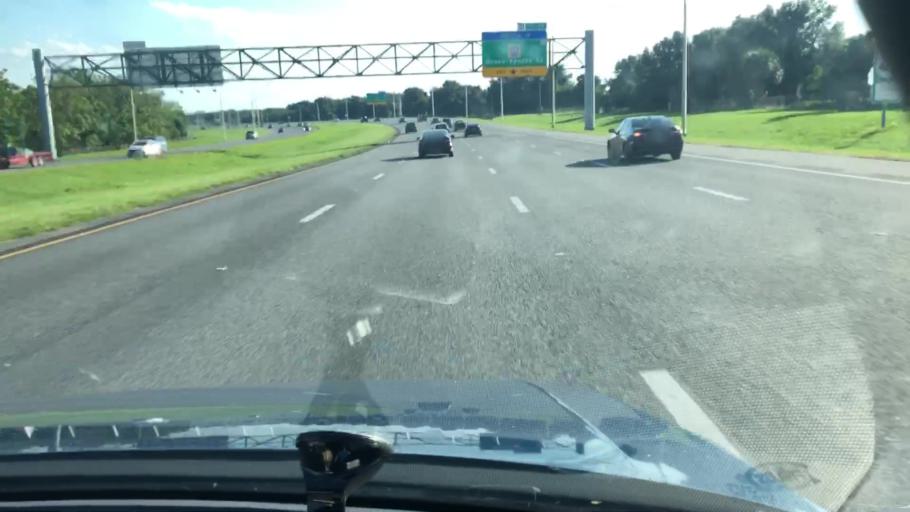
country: US
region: Florida
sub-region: Orange County
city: Paradise Heights
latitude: 28.6424
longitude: -81.5438
